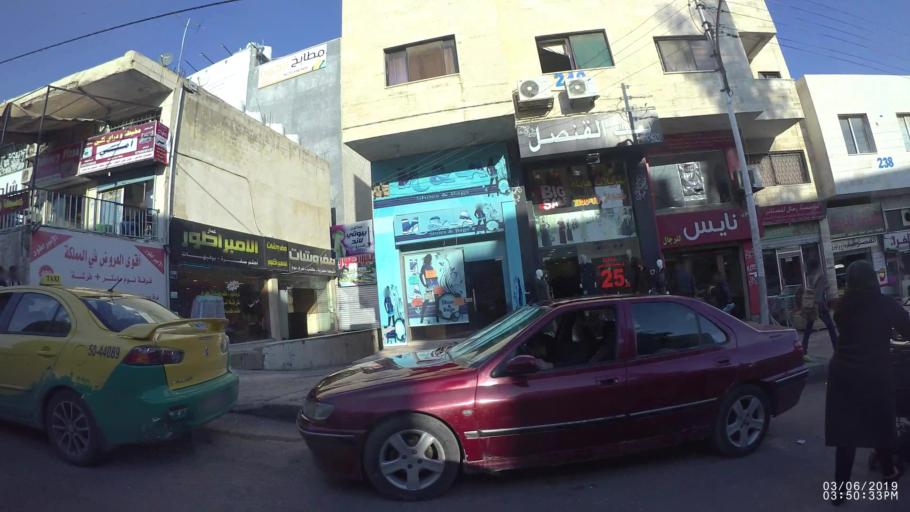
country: JO
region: Amman
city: Amman
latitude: 31.9757
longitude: 35.9497
